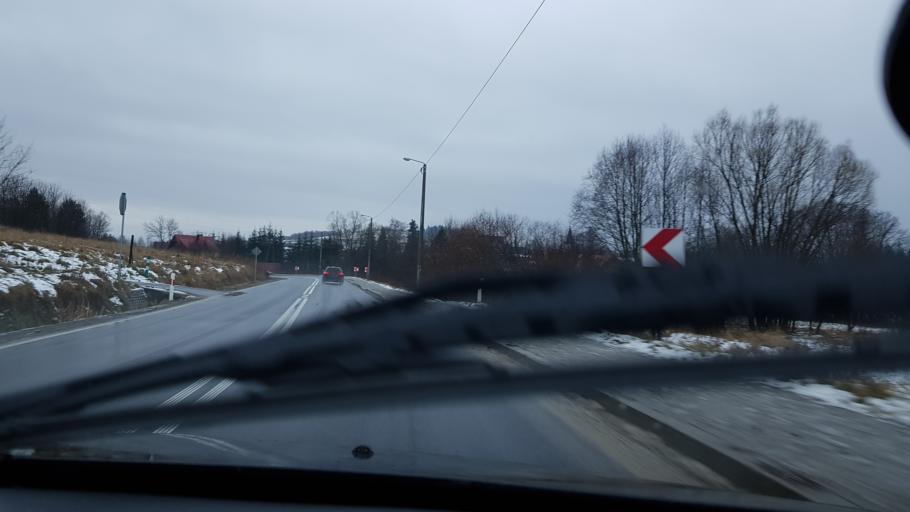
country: PL
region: Lesser Poland Voivodeship
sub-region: Powiat nowotarski
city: Sieniawa
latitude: 49.5011
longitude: 19.8832
